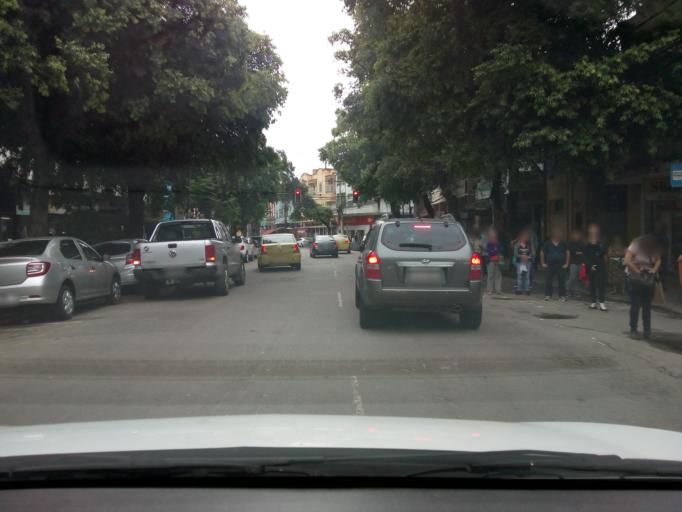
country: BR
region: Rio de Janeiro
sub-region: Rio De Janeiro
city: Rio de Janeiro
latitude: -22.9024
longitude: -43.2181
